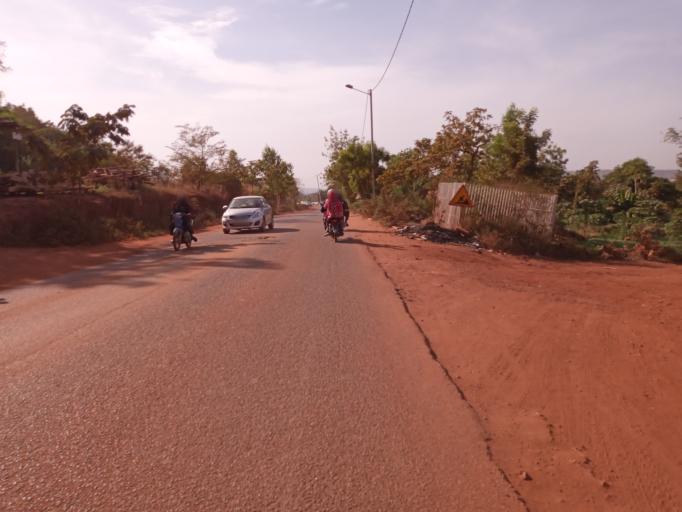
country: ML
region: Bamako
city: Bamako
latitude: 12.6294
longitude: -7.9505
